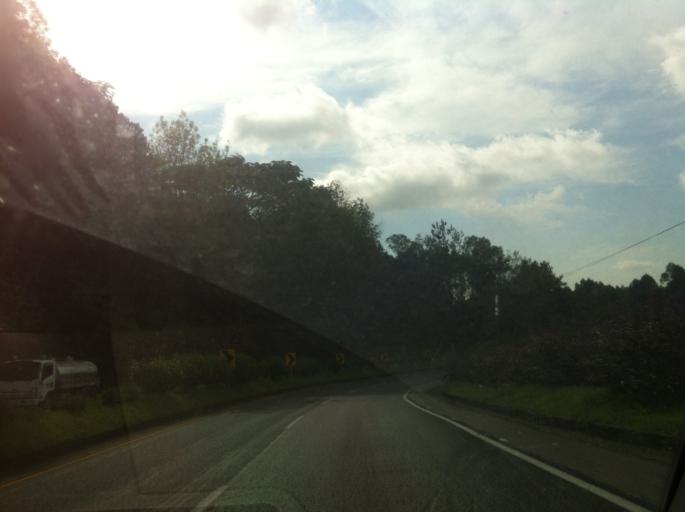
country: CO
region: Quindio
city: Filandia
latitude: 4.7163
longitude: -75.6208
